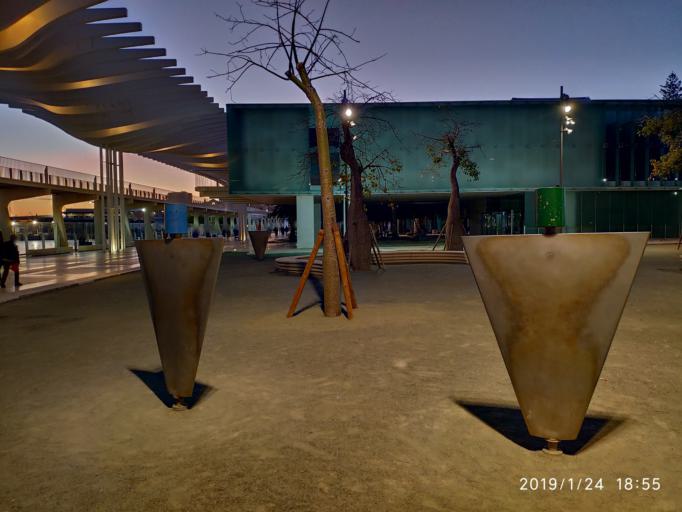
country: ES
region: Andalusia
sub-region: Provincia de Malaga
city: Malaga
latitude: 36.7181
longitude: -4.4163
